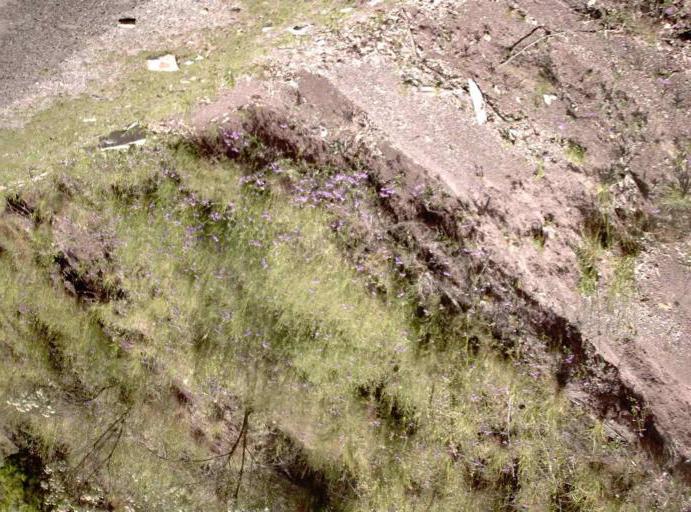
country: AU
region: New South Wales
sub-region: Bombala
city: Bombala
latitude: -37.6163
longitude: 148.8904
